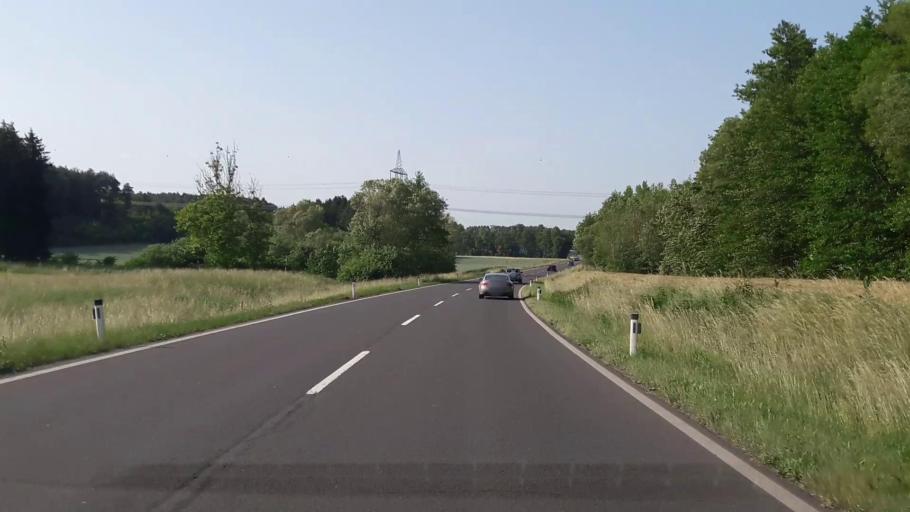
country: AT
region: Burgenland
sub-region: Politischer Bezirk Oberwart
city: Kemeten
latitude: 47.2635
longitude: 16.1519
